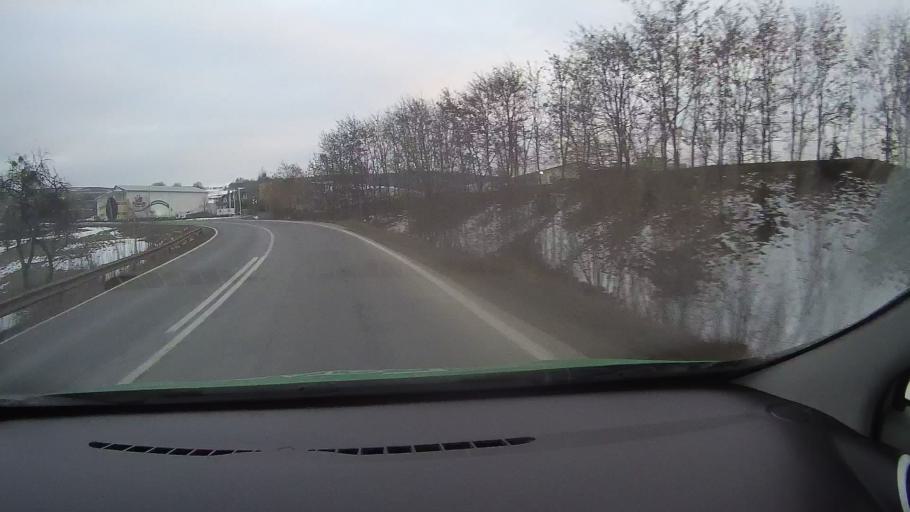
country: RO
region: Harghita
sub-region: Comuna Lupeni
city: Lupeni
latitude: 46.3561
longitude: 25.2394
